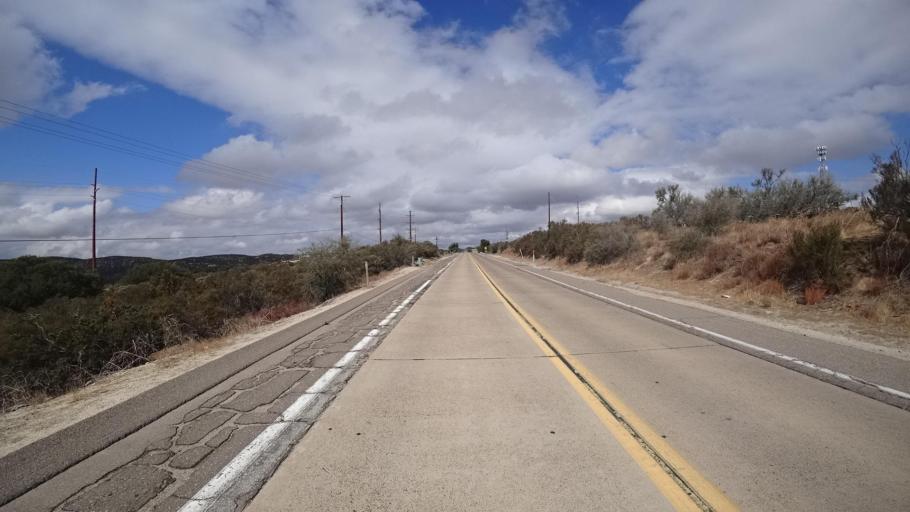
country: US
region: California
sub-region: San Diego County
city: Campo
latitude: 32.6974
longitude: -116.3519
